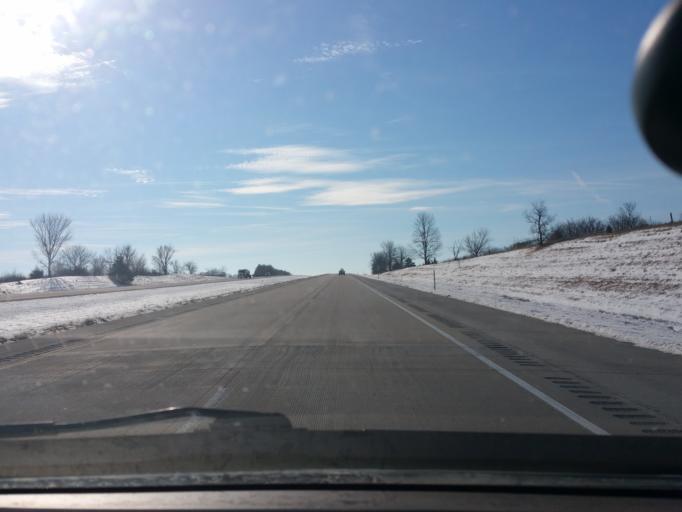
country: US
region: Iowa
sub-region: Decatur County
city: Leon
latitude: 40.7860
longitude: -93.8353
